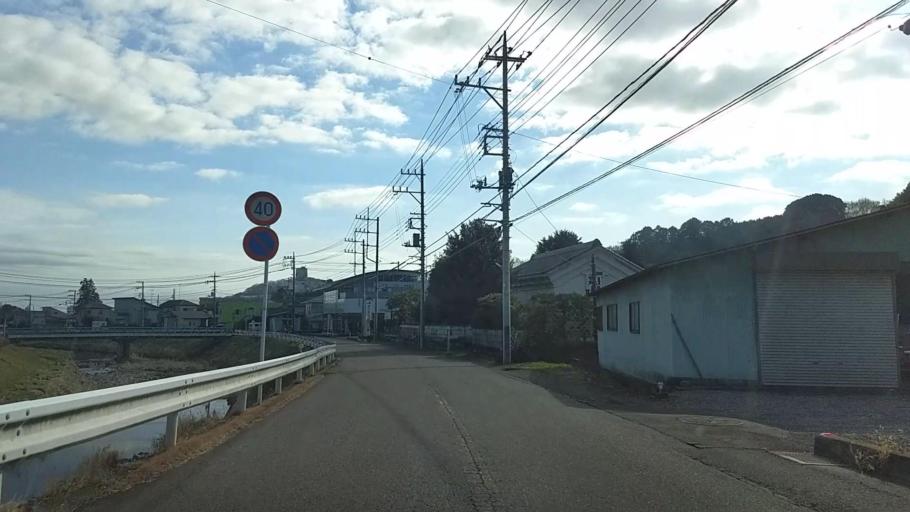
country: JP
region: Kanagawa
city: Isehara
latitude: 35.4358
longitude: 139.3069
